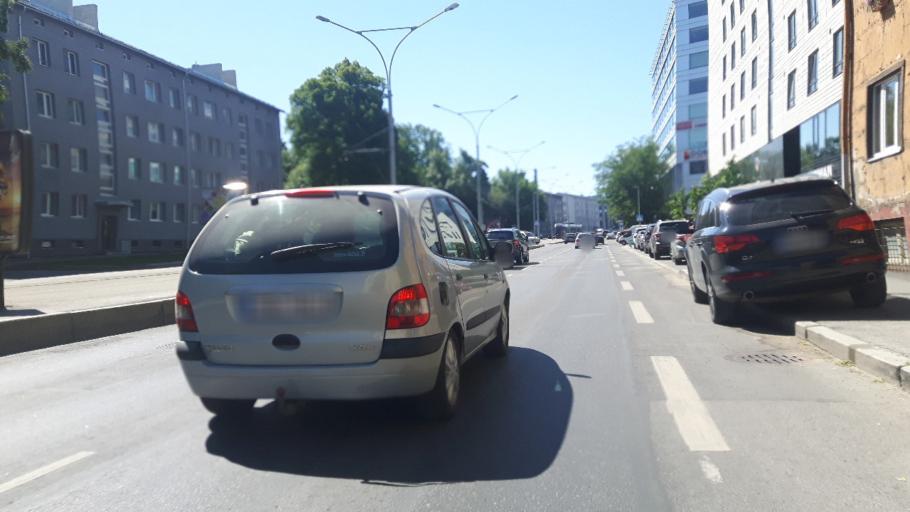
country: EE
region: Harju
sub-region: Tallinna linn
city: Tallinn
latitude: 59.4130
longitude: 24.7385
